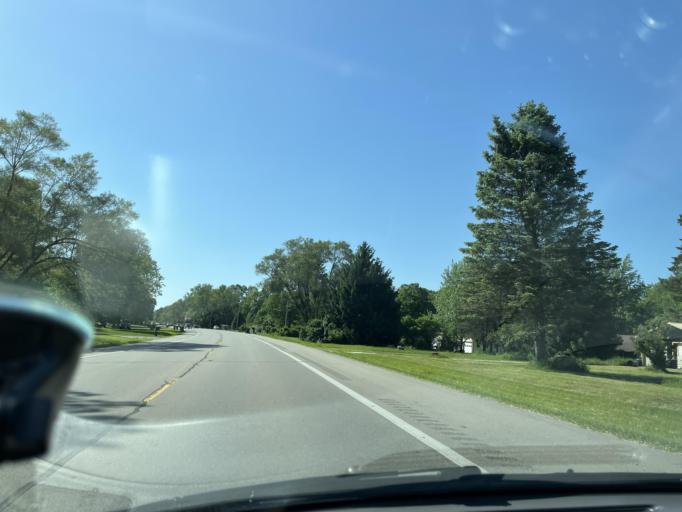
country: US
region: Michigan
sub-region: Barry County
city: Hastings
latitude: 42.6537
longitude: -85.3444
